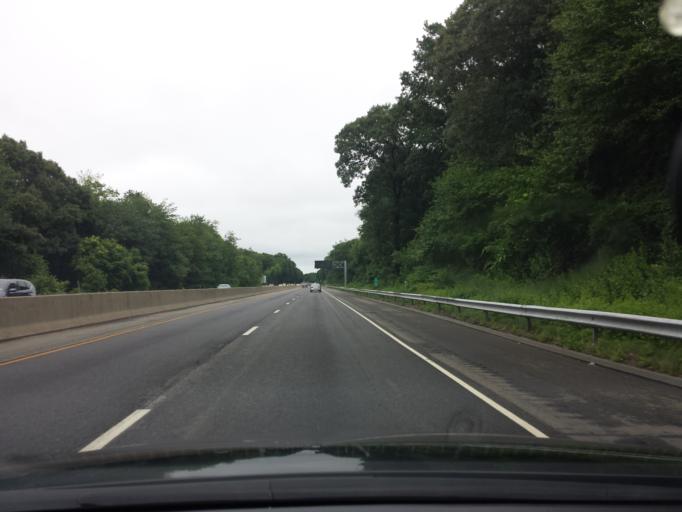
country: US
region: Connecticut
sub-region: Middlesex County
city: Saybrook Manor
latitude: 41.2931
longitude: -72.4092
